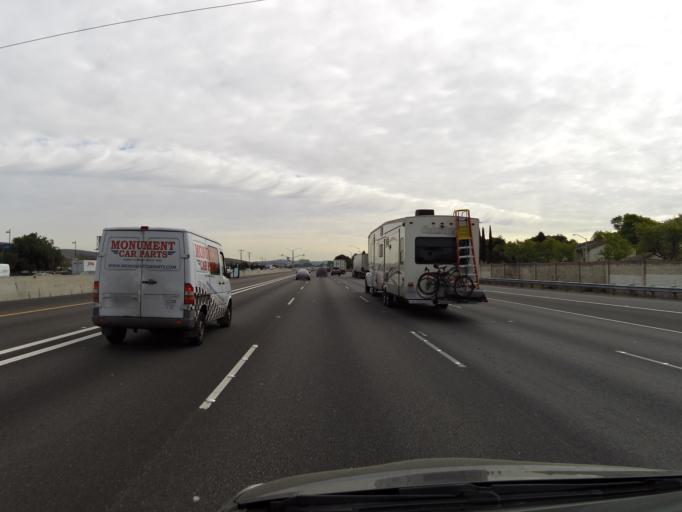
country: US
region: California
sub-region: Alameda County
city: Pleasanton
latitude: 37.7009
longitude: -121.8675
